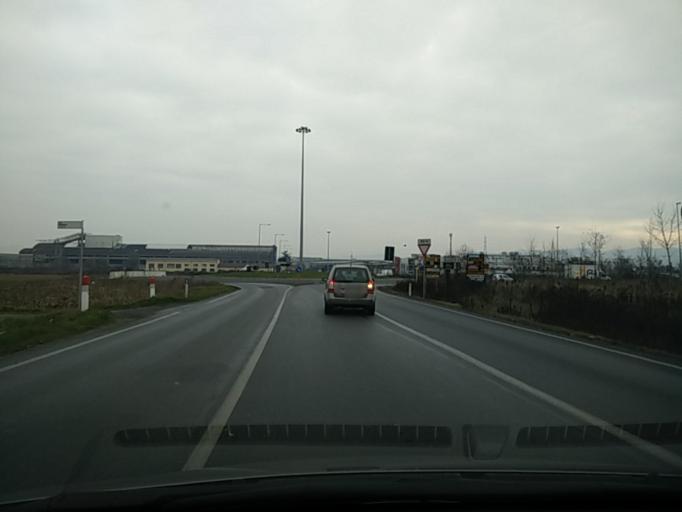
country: IT
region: Piedmont
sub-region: Provincia di Torino
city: Settimo Torinese
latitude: 45.1462
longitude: 7.7393
